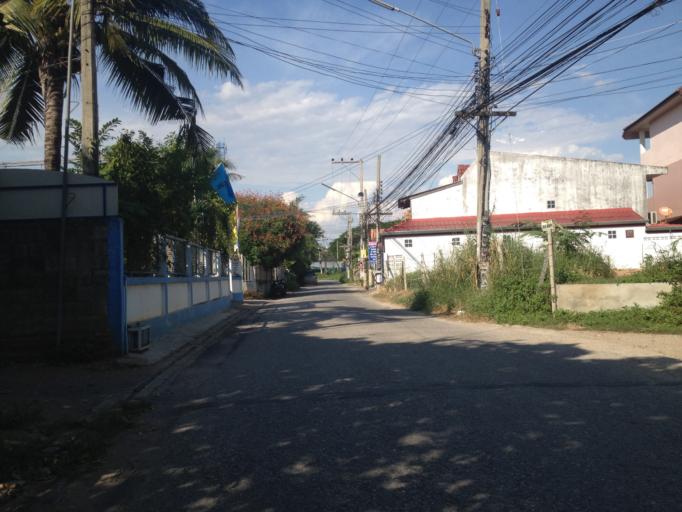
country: TH
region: Chiang Mai
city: Chiang Mai
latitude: 18.7576
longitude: 98.9836
